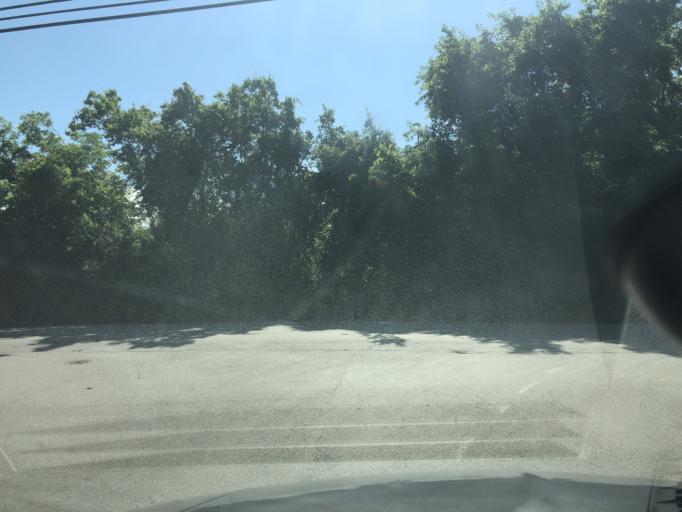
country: US
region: Texas
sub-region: Tarrant County
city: Euless
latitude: 32.8113
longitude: -97.0205
